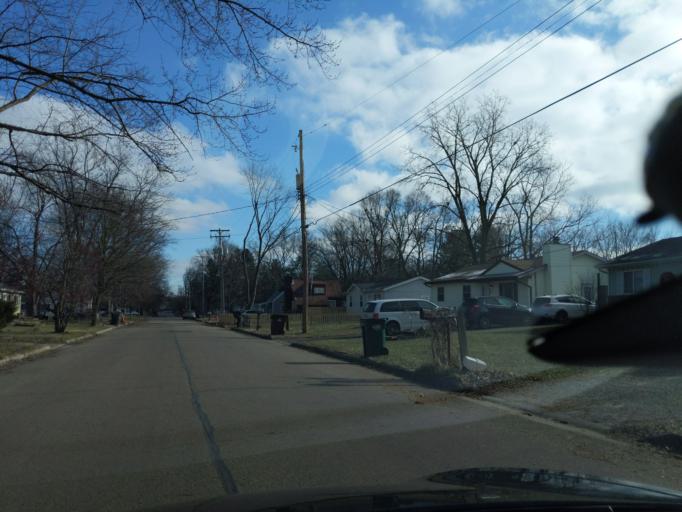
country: US
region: Michigan
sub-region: Ingham County
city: Lansing
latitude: 42.6820
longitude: -84.5897
